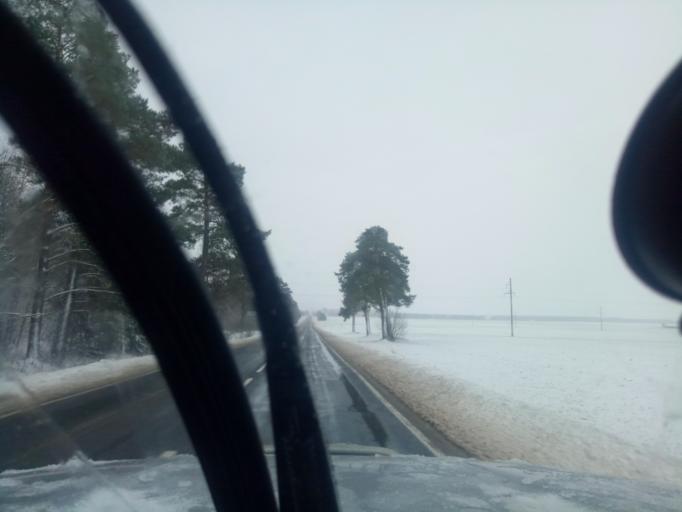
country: BY
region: Minsk
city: Haradzyeya
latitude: 53.3736
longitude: 26.5100
